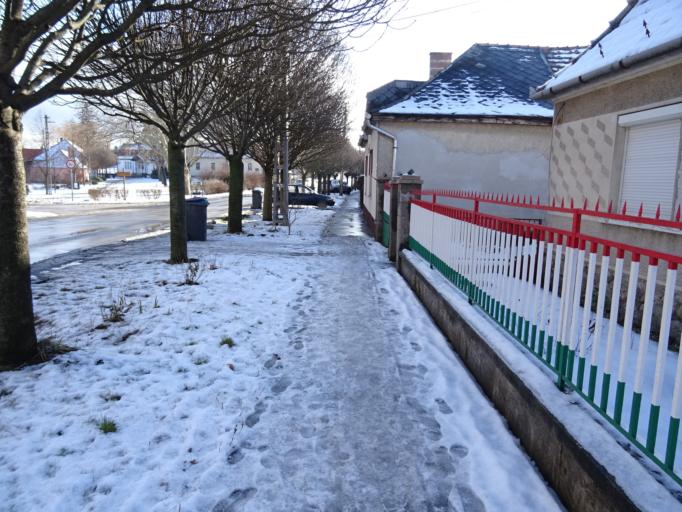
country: HU
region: Komarom-Esztergom
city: Oroszlany
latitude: 47.4883
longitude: 18.3221
